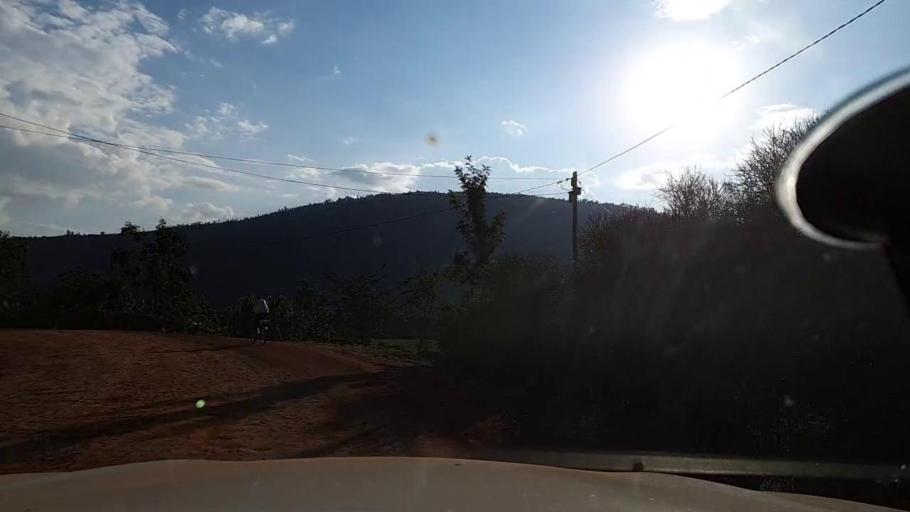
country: RW
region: Kigali
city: Kigali
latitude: -1.9203
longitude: 29.9896
